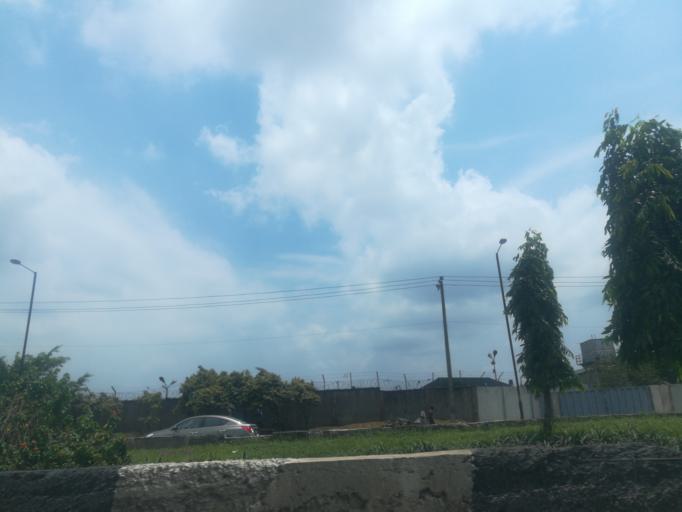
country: NG
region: Lagos
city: Ojota
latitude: 6.5863
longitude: 3.3885
